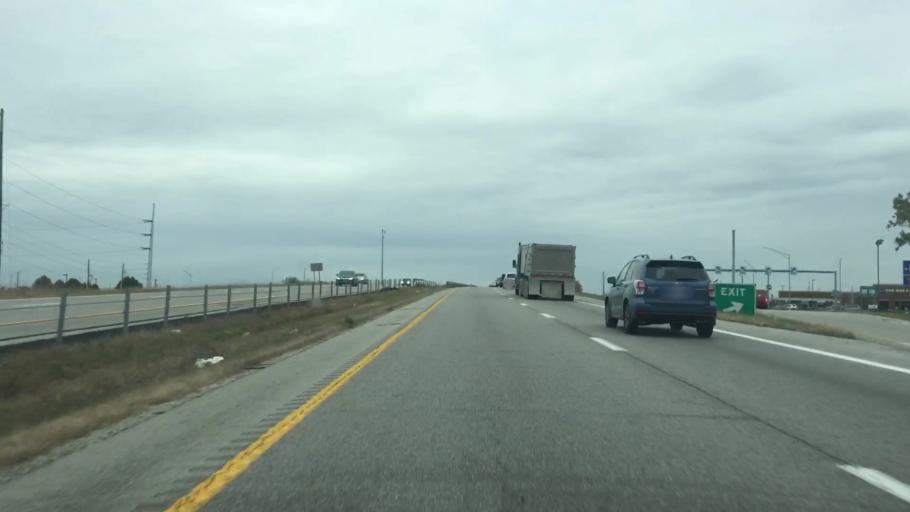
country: US
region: Missouri
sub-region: Jackson County
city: Lees Summit
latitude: 38.9239
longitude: -94.4033
